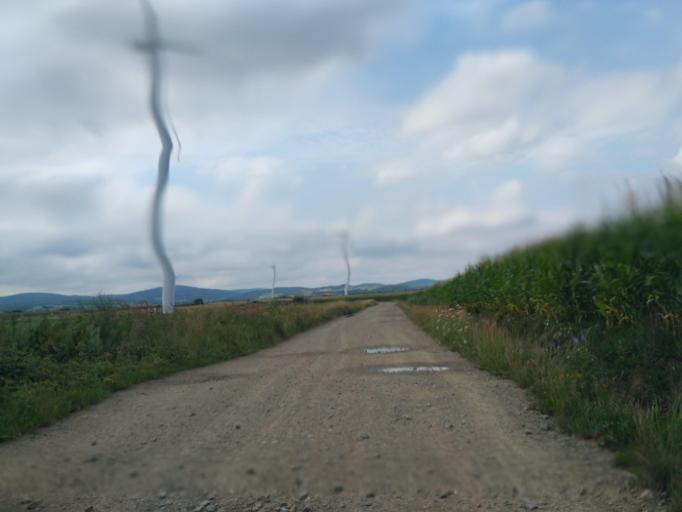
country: PL
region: Subcarpathian Voivodeship
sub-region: Powiat krosnienski
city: Rymanow
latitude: 49.6126
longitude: 21.8455
